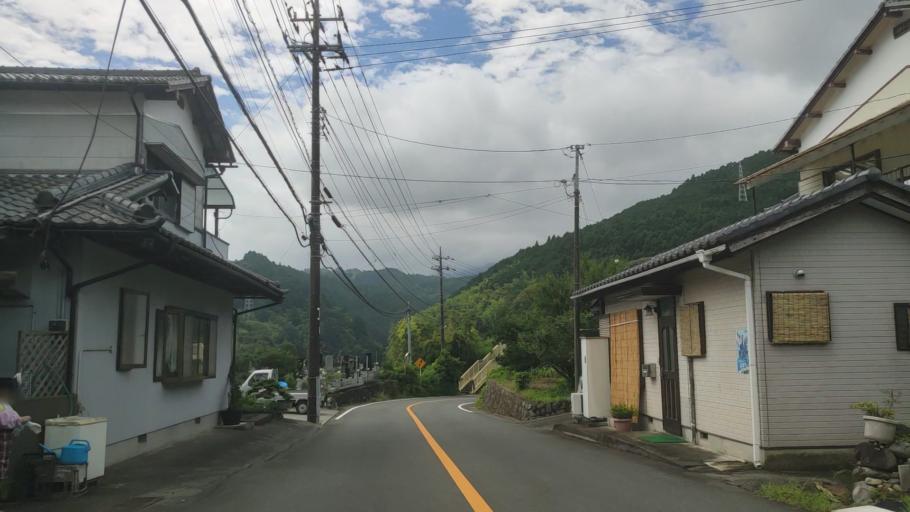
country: JP
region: Shizuoka
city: Fujinomiya
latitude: 35.2221
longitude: 138.5147
